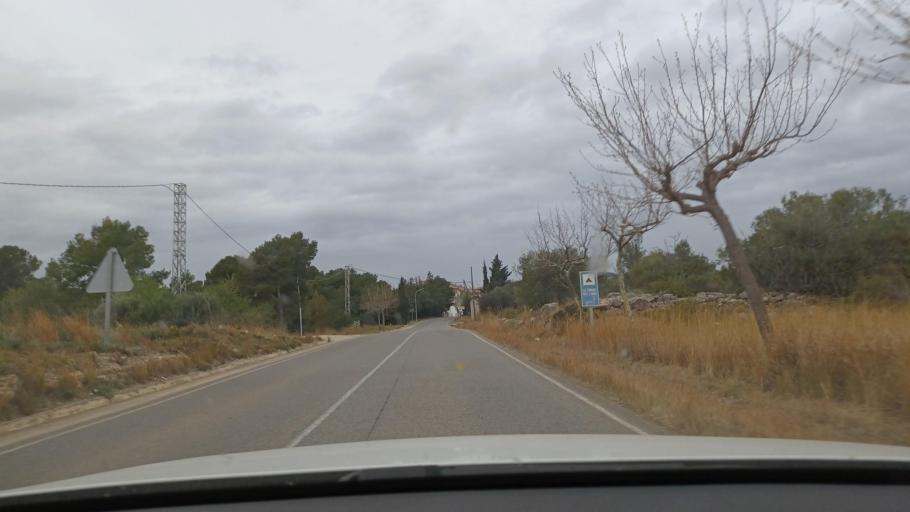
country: ES
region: Valencia
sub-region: Provincia de Castello
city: Rosell
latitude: 40.6302
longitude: 0.2895
